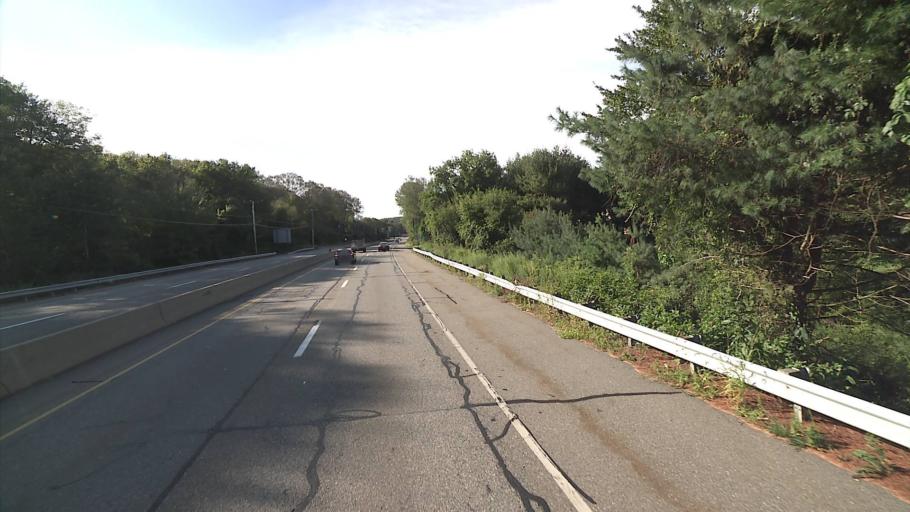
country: US
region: Connecticut
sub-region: New London County
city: Uncasville
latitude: 41.4090
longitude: -72.1069
